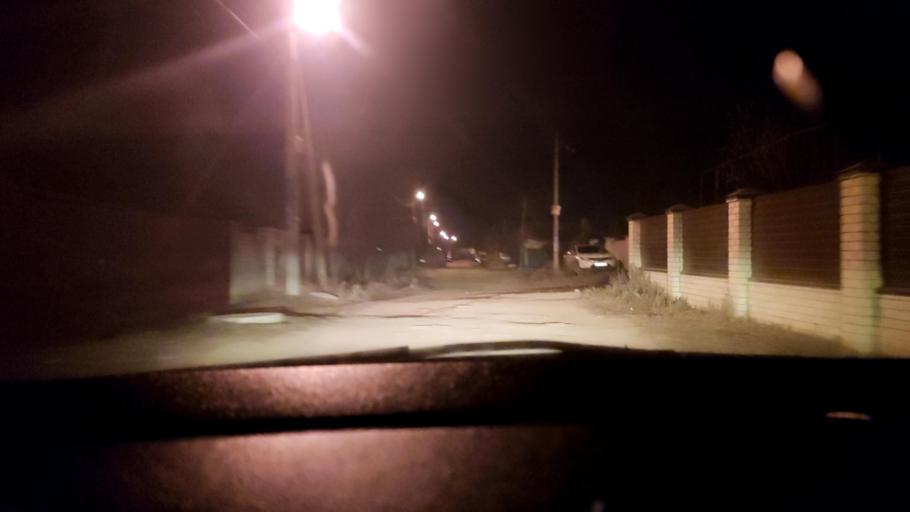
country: RU
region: Voronezj
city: Pridonskoy
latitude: 51.6527
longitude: 39.0865
